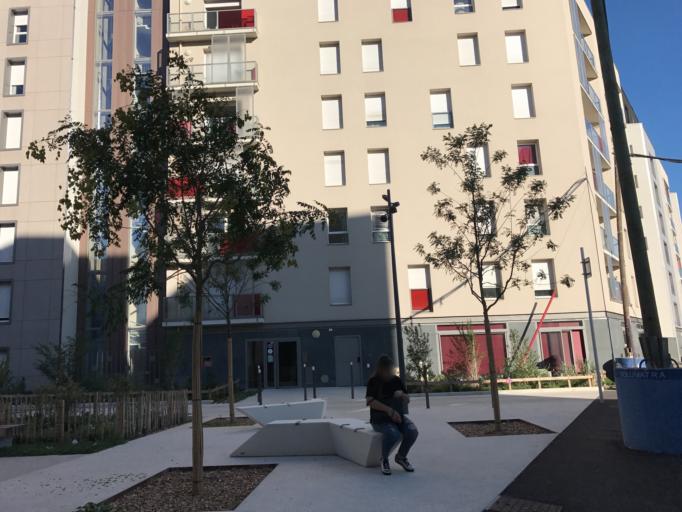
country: FR
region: Rhone-Alpes
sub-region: Departement du Rhone
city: Lyon
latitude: 45.7402
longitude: 4.8353
